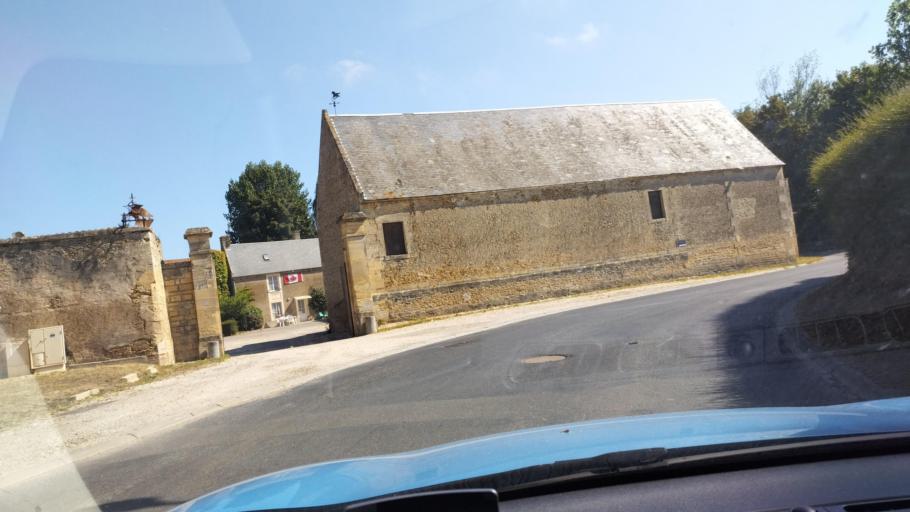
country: FR
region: Lower Normandy
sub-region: Departement du Calvados
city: Bernieres-sur-Mer
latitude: 49.3060
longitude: -0.4086
